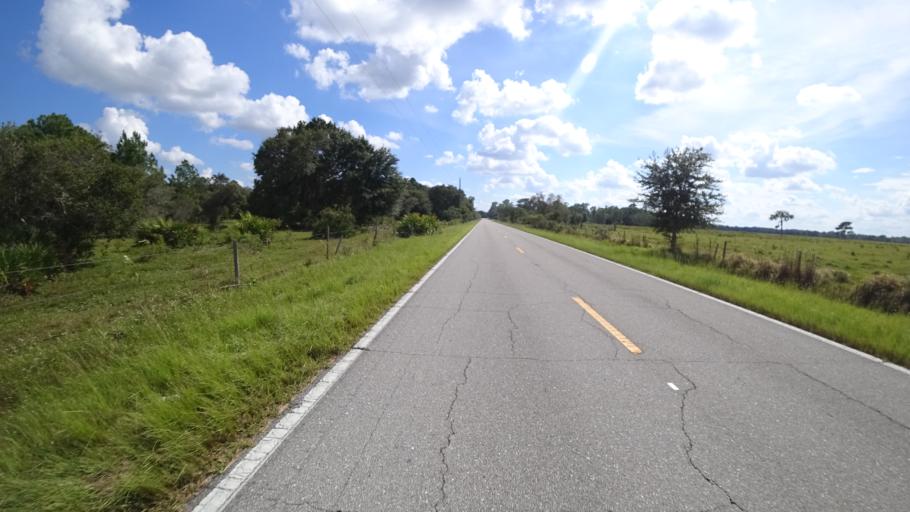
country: US
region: Florida
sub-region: Hardee County
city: Wauchula
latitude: 27.4995
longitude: -82.0711
